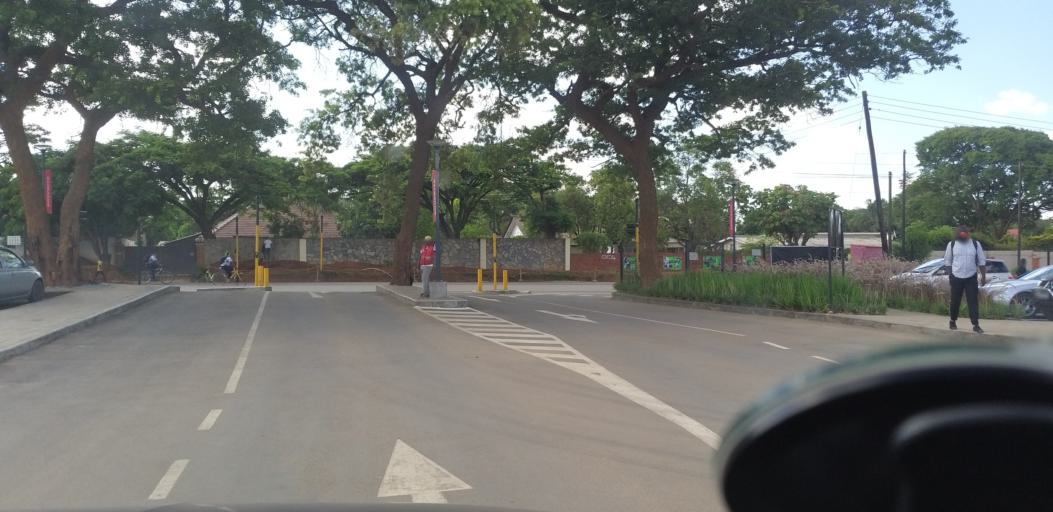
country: ZM
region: Lusaka
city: Lusaka
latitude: -15.4316
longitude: 28.3416
